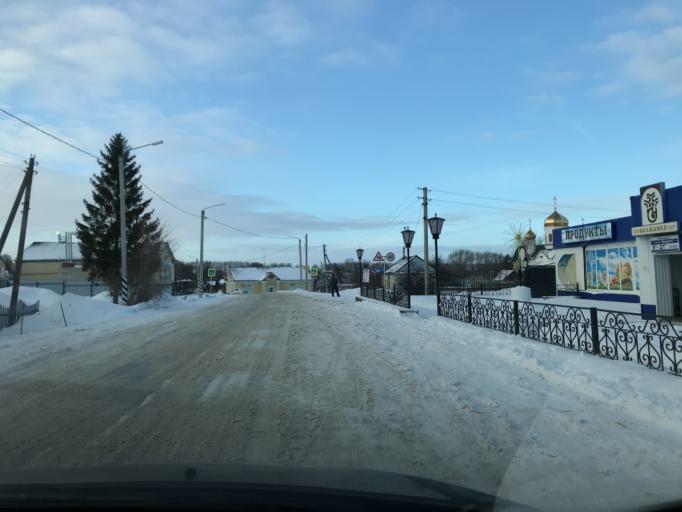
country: RU
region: Ulyanovsk
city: Undory
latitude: 54.6082
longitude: 48.3953
